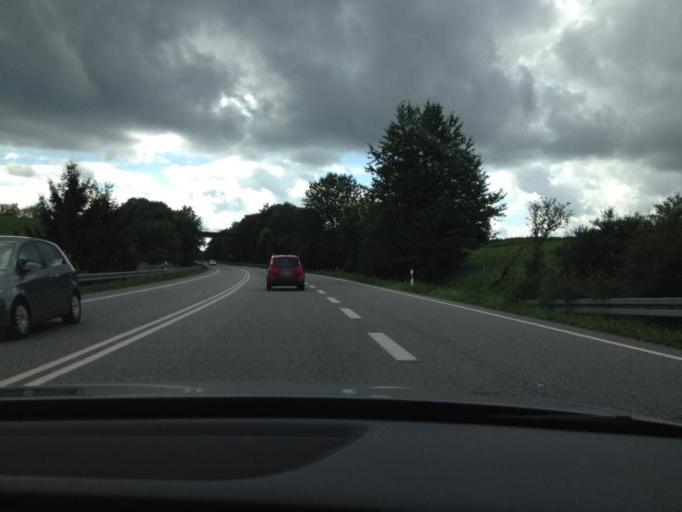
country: DE
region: Saarland
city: Sankt Wendel
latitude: 49.4795
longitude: 7.1444
